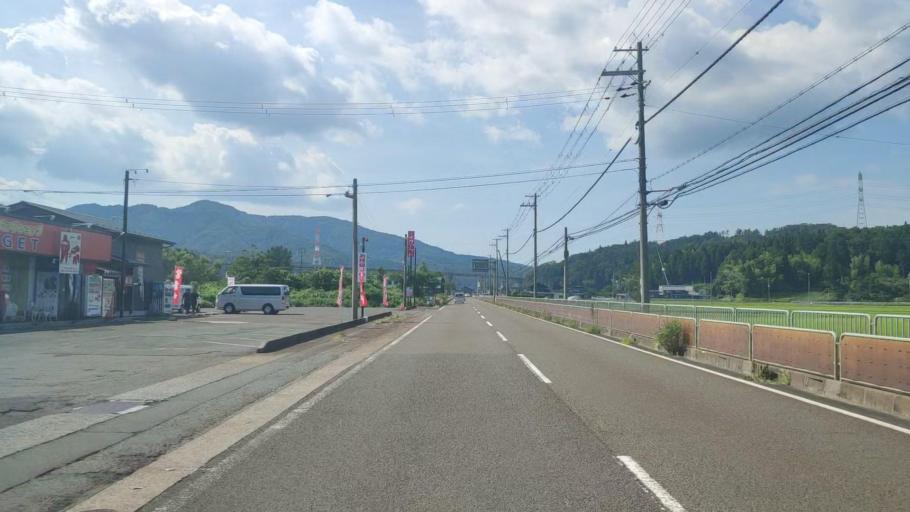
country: JP
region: Fukui
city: Tsuruga
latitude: 35.5257
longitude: 136.1597
